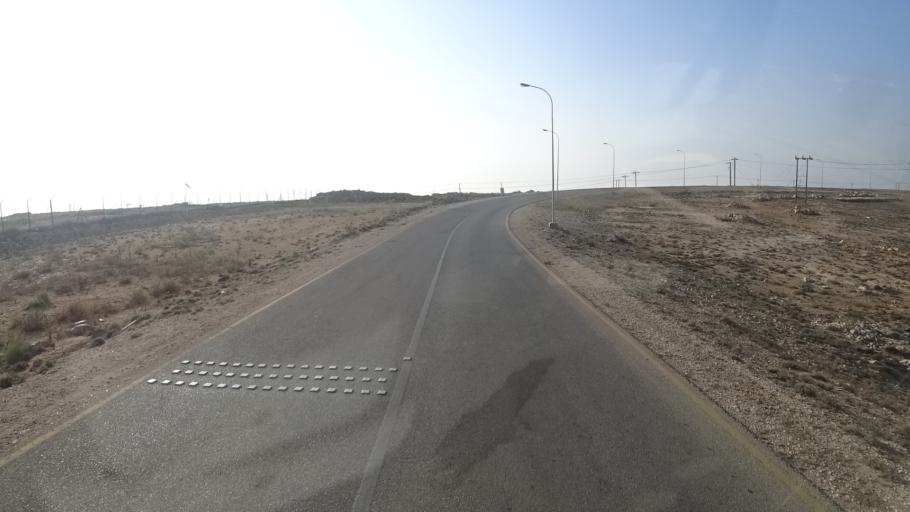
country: YE
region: Al Mahrah
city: Hawf
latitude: 16.7777
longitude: 53.2322
